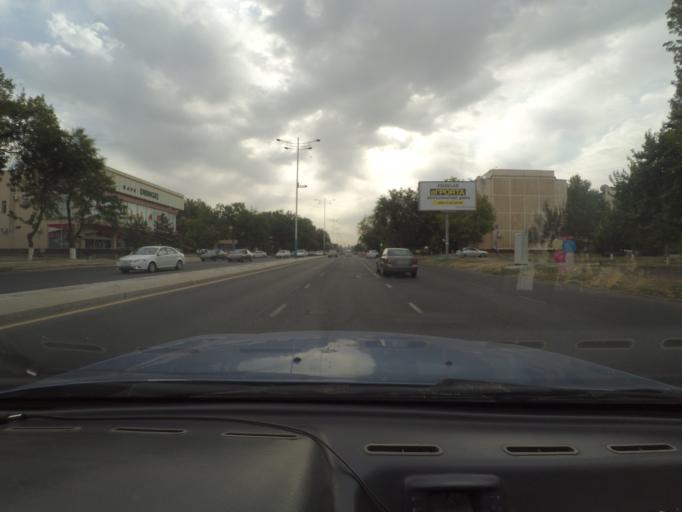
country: UZ
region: Toshkent
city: Salor
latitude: 41.3549
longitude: 69.3615
